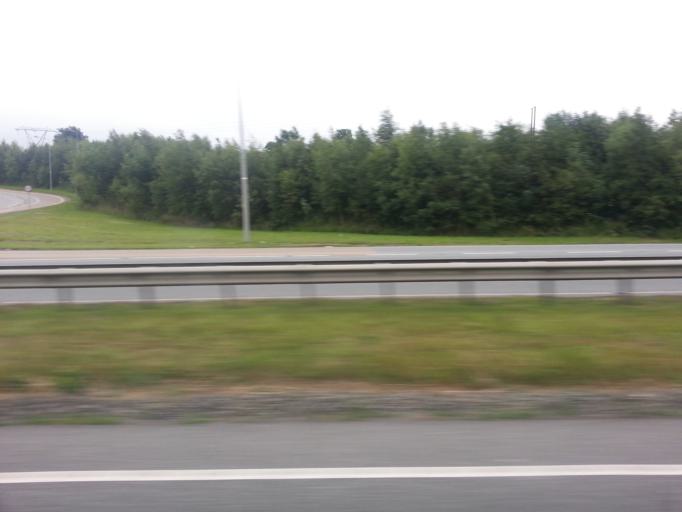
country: IE
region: Leinster
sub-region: South Dublin
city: Newcastle
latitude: 53.2680
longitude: -6.5223
